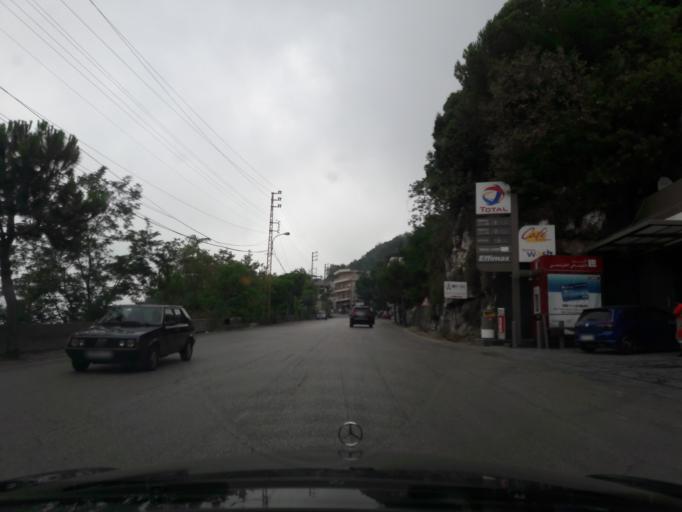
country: LB
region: Mont-Liban
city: Djounie
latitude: 33.9176
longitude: 35.6666
